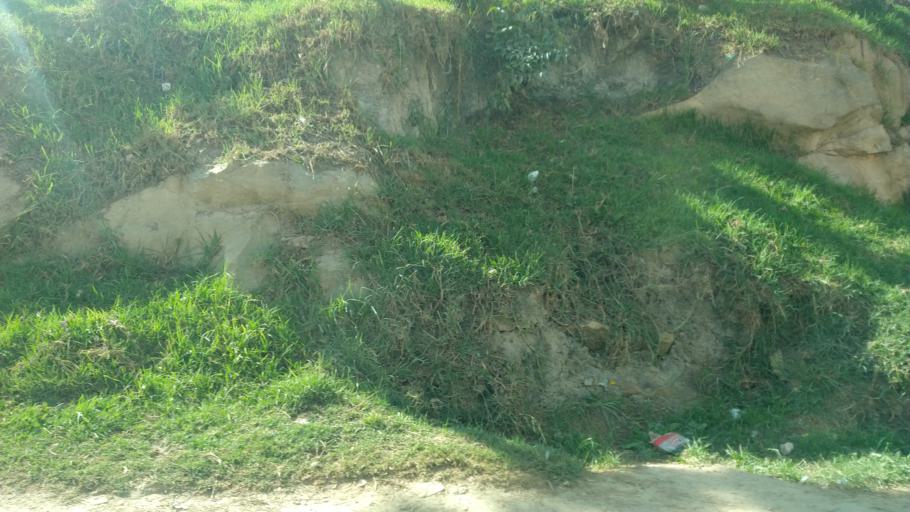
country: CO
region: Cundinamarca
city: Soacha
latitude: 4.5643
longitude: -74.1871
